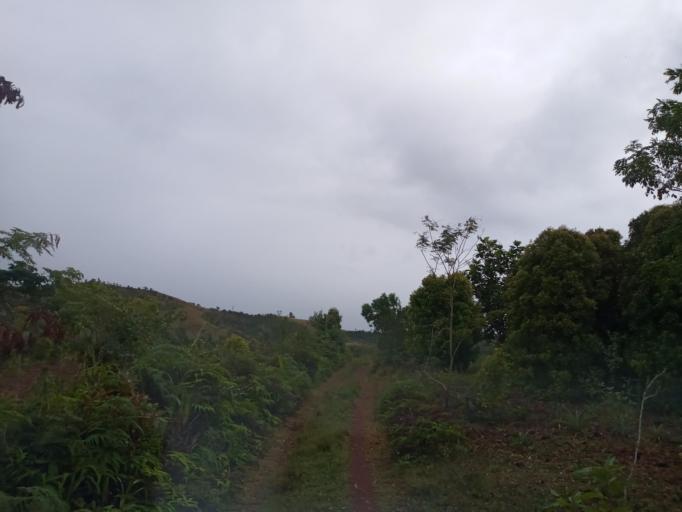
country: MG
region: Atsimo-Atsinanana
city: Vohipaho
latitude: -23.9931
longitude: 47.4026
